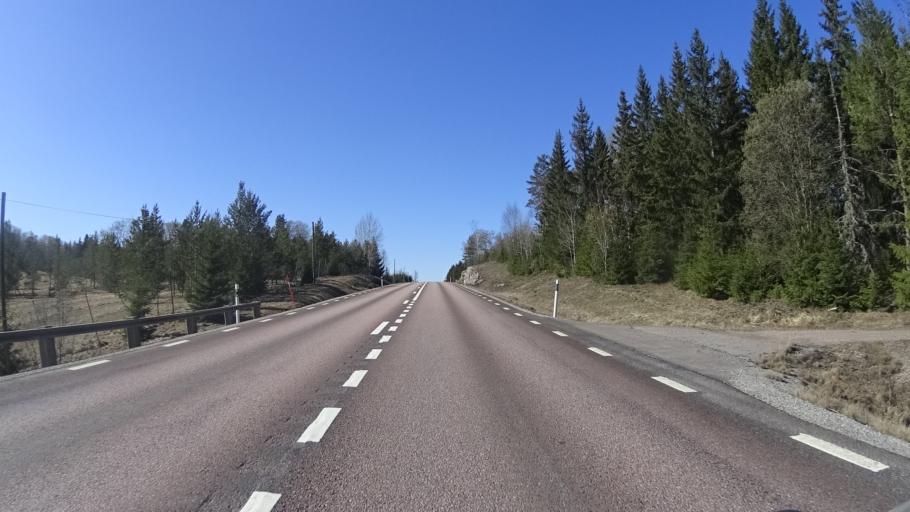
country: SE
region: Vaermland
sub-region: Sunne Kommun
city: Sunne
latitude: 59.6202
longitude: 12.9709
